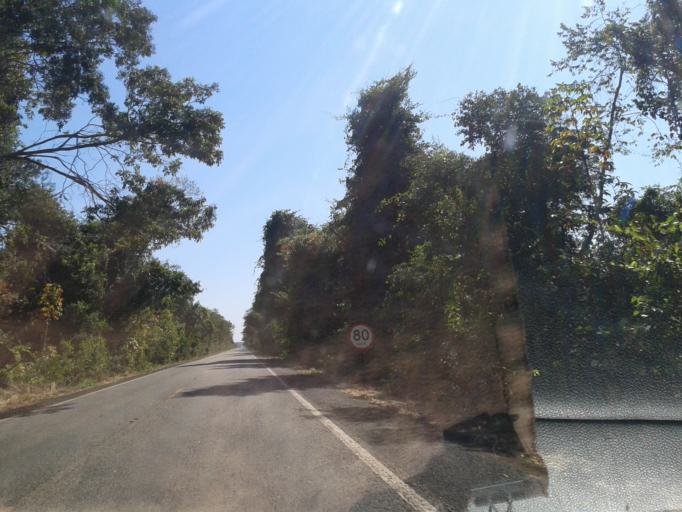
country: BR
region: Goias
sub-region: Crixas
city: Crixas
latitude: -14.0124
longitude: -50.3259
